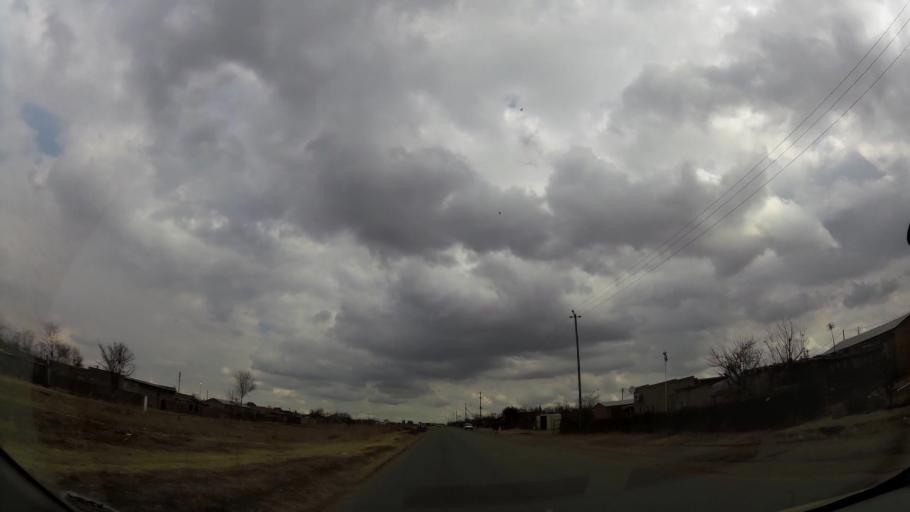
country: ZA
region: Orange Free State
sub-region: Fezile Dabi District Municipality
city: Sasolburg
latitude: -26.8512
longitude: 27.8743
